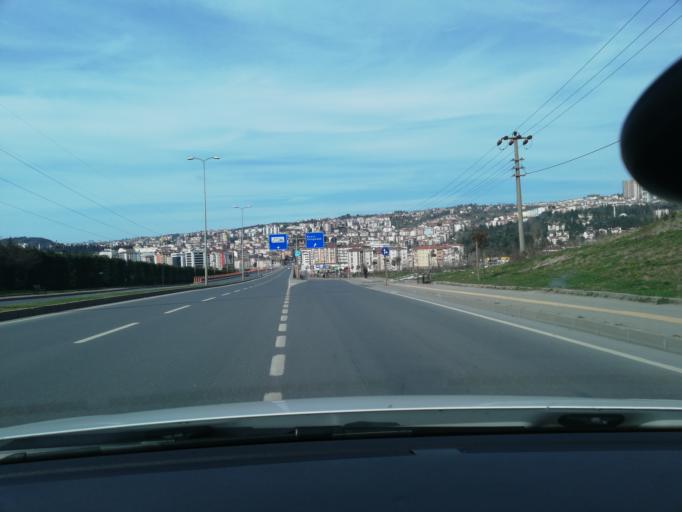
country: TR
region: Zonguldak
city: Eregli
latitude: 41.2651
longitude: 31.4353
